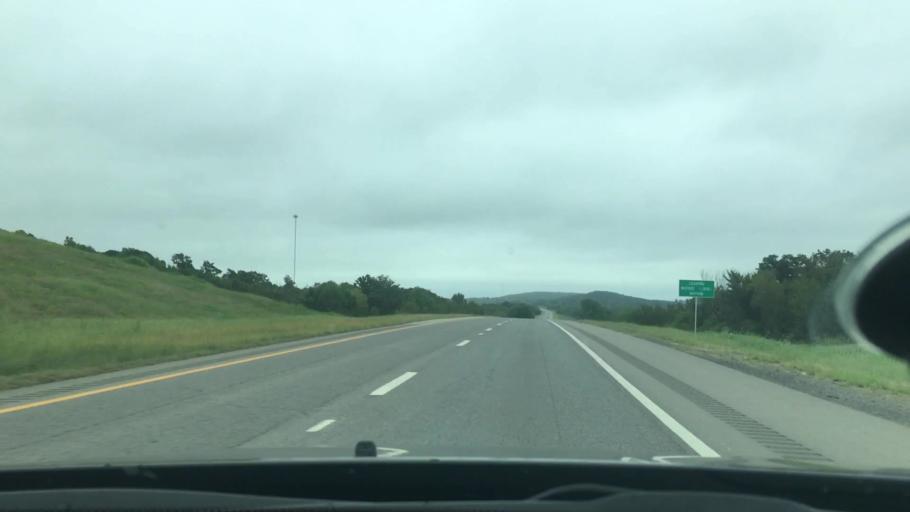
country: US
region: Oklahoma
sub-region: McIntosh County
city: Checotah
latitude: 35.4572
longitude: -95.4242
